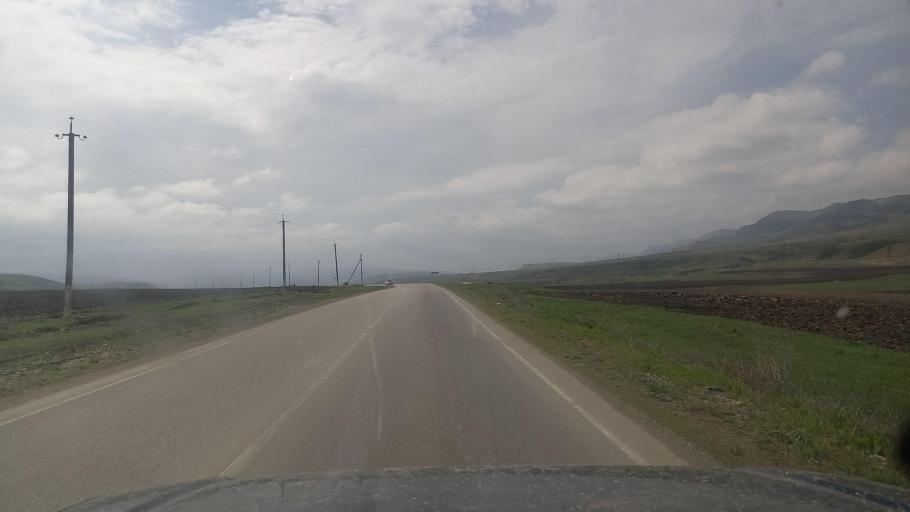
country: RU
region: Kabardino-Balkariya
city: Kamennomostskoye
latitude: 43.7284
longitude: 43.1068
